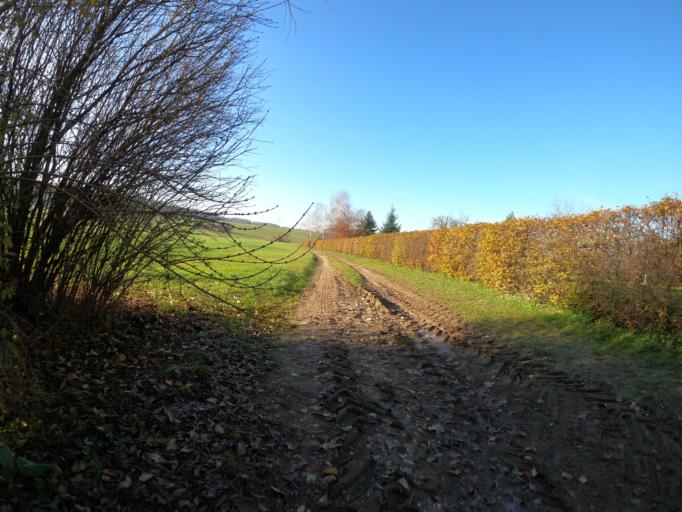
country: DE
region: Baden-Wuerttemberg
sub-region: Regierungsbezirk Stuttgart
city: Albershausen
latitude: 48.7064
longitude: 9.5558
